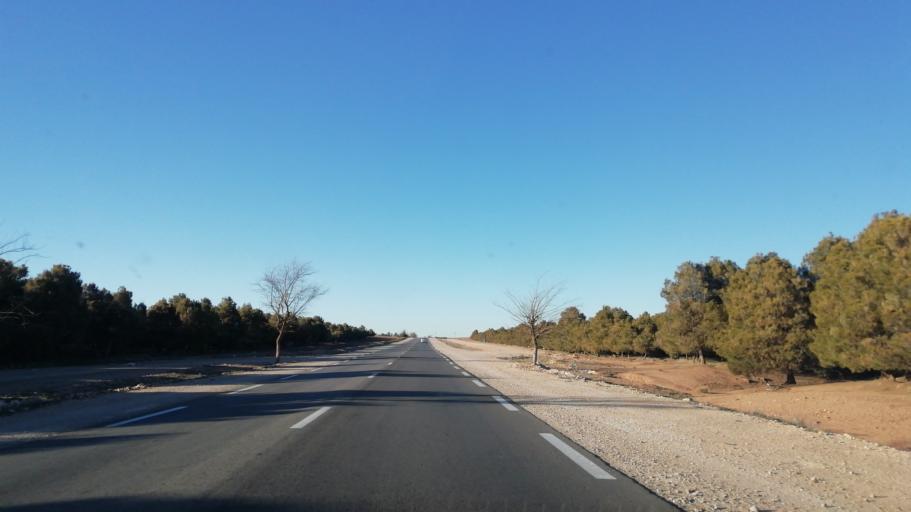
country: DZ
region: Tlemcen
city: Sebdou
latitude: 34.5133
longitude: -1.2846
